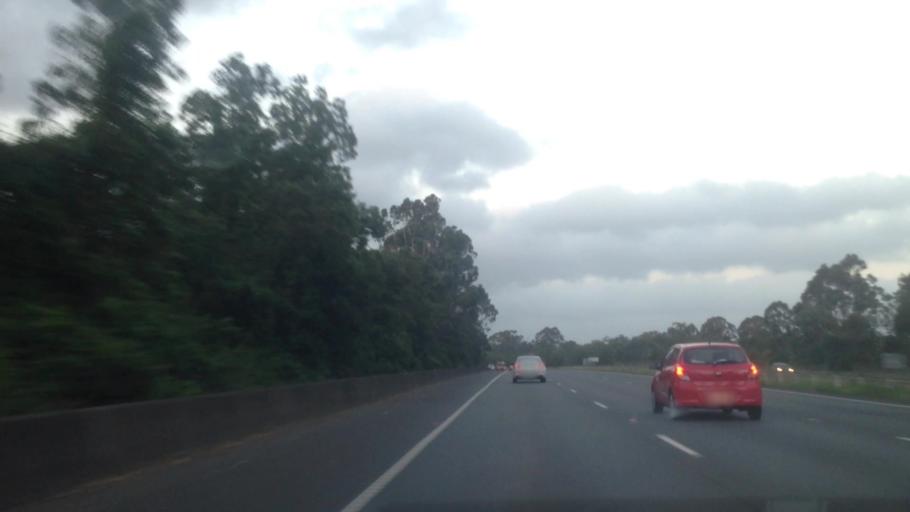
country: AU
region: New South Wales
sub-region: Wyong Shire
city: Chittaway Bay
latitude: -33.3333
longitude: 151.3798
